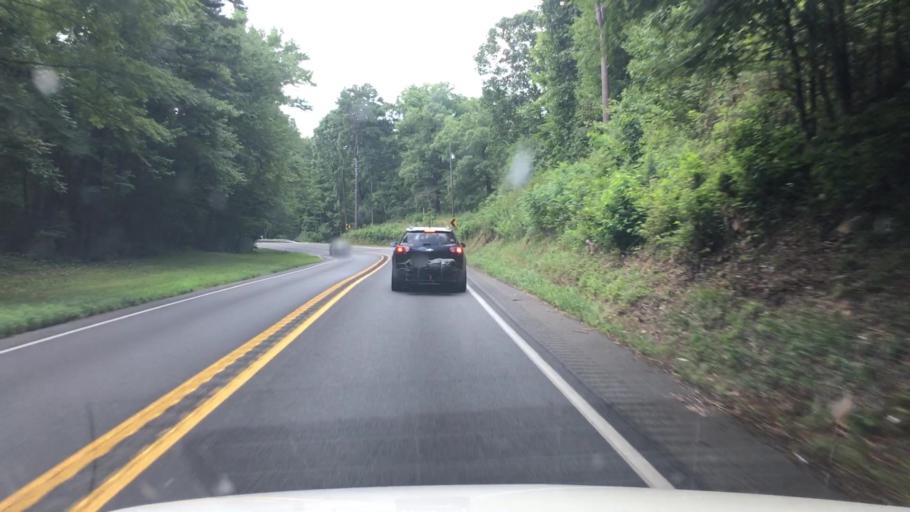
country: US
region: Arkansas
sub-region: Garland County
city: Lake Hamilton
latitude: 34.3426
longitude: -93.1839
